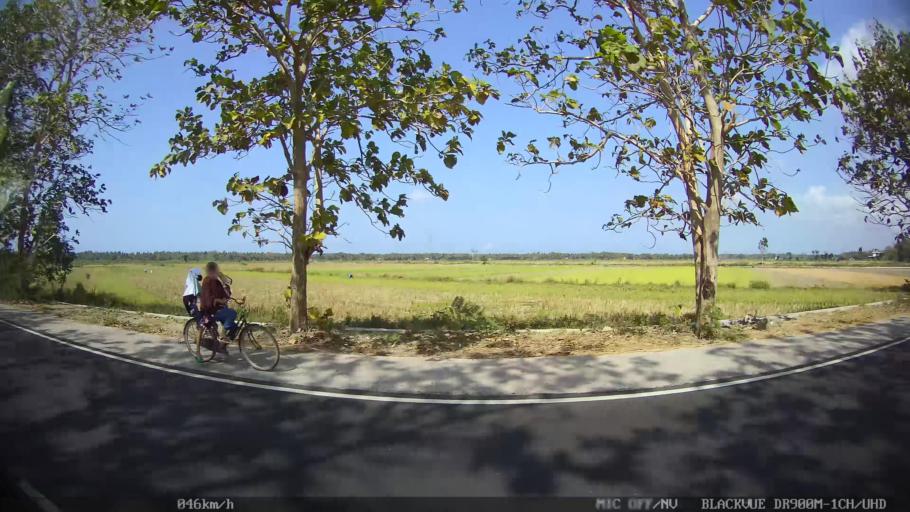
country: ID
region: Daerah Istimewa Yogyakarta
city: Srandakan
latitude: -7.8981
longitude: 110.1638
